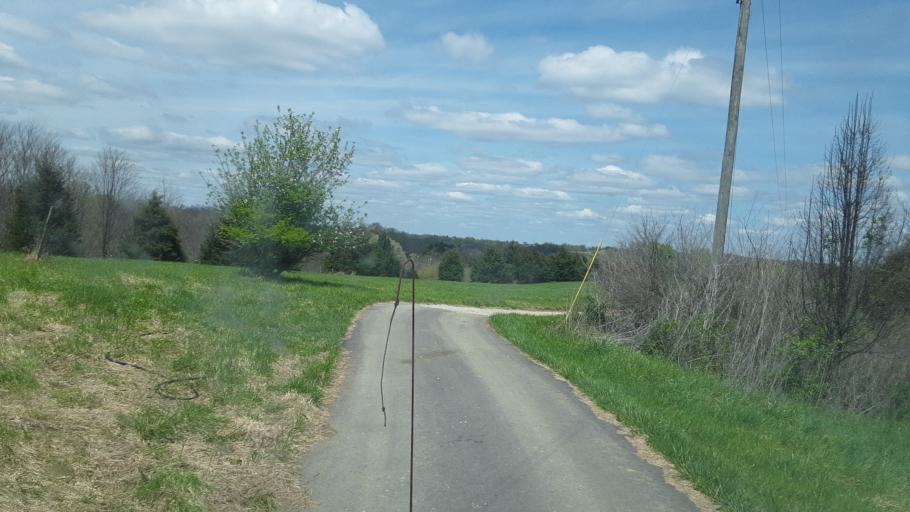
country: US
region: Kentucky
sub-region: Owen County
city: Owenton
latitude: 38.6798
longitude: -84.7840
